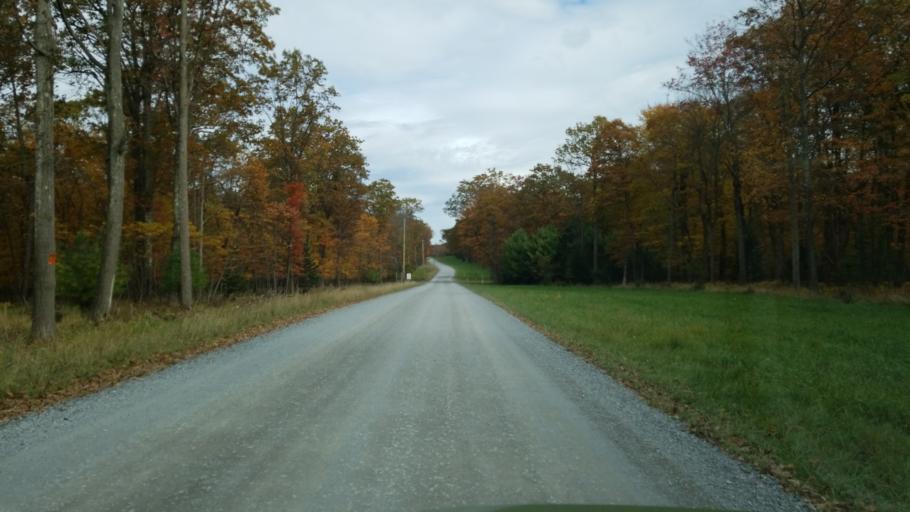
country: US
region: Pennsylvania
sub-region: Clearfield County
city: Clearfield
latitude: 41.1554
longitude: -78.4602
